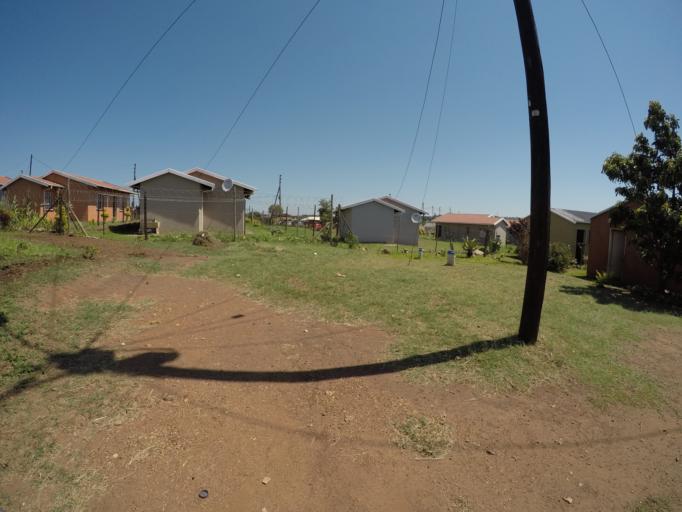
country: ZA
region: KwaZulu-Natal
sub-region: uThungulu District Municipality
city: Empangeni
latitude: -28.7644
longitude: 31.8793
